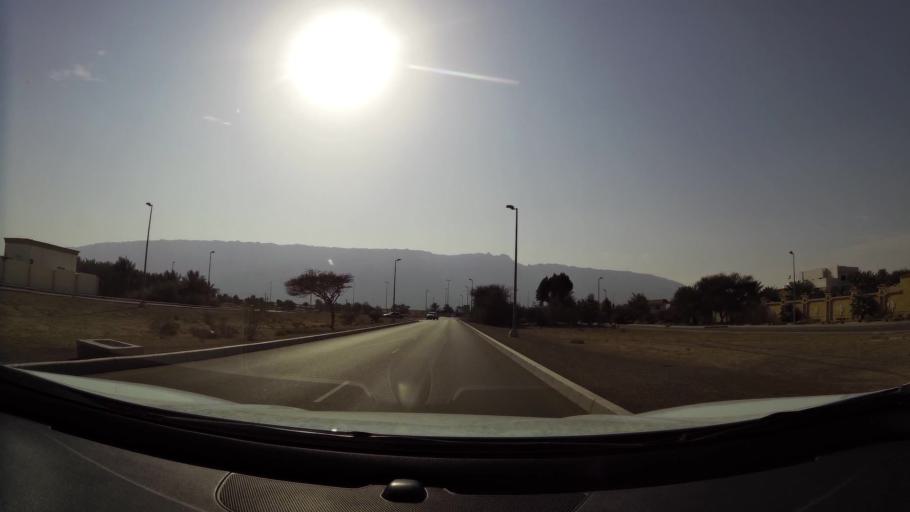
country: AE
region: Abu Dhabi
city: Al Ain
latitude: 24.0647
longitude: 55.8403
